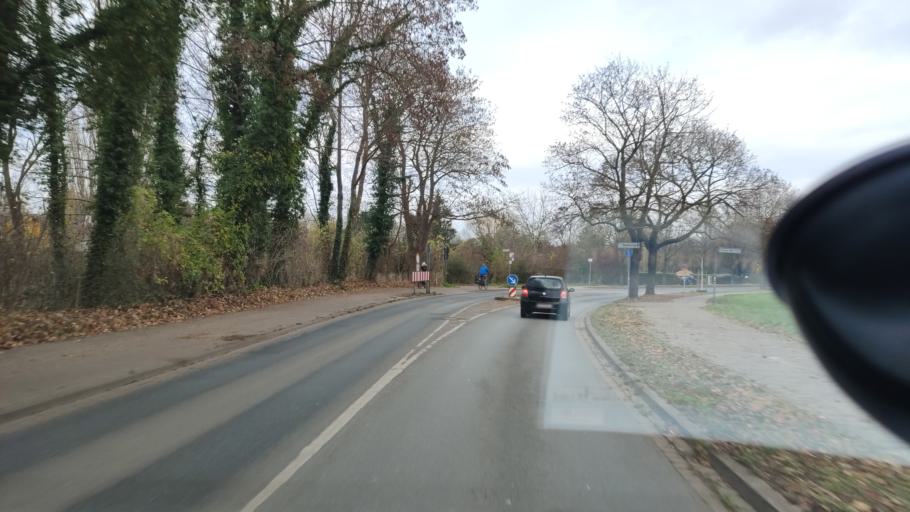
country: DE
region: Lower Saxony
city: Hemmingen
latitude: 52.3338
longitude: 9.7563
